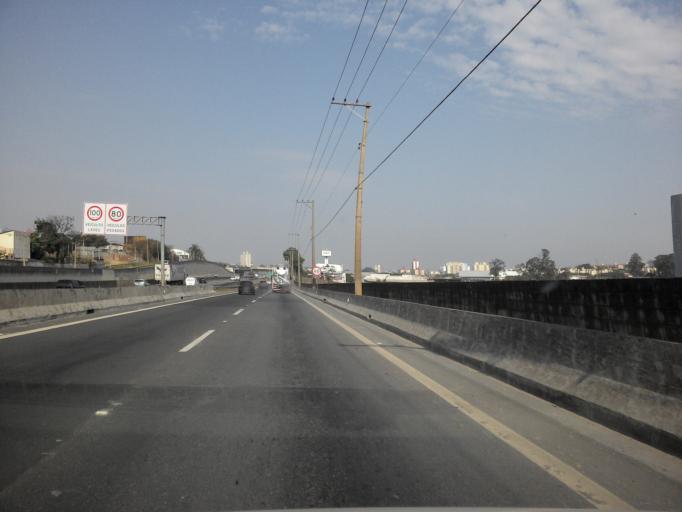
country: BR
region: Sao Paulo
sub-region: Campinas
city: Campinas
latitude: -22.9051
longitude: -47.1072
